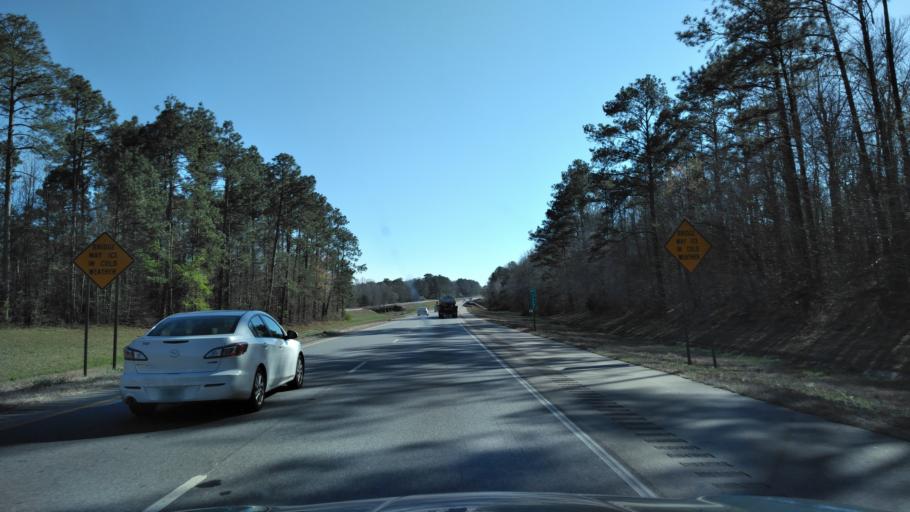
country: US
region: Alabama
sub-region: Butler County
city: Greenville
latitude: 31.8150
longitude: -86.6665
